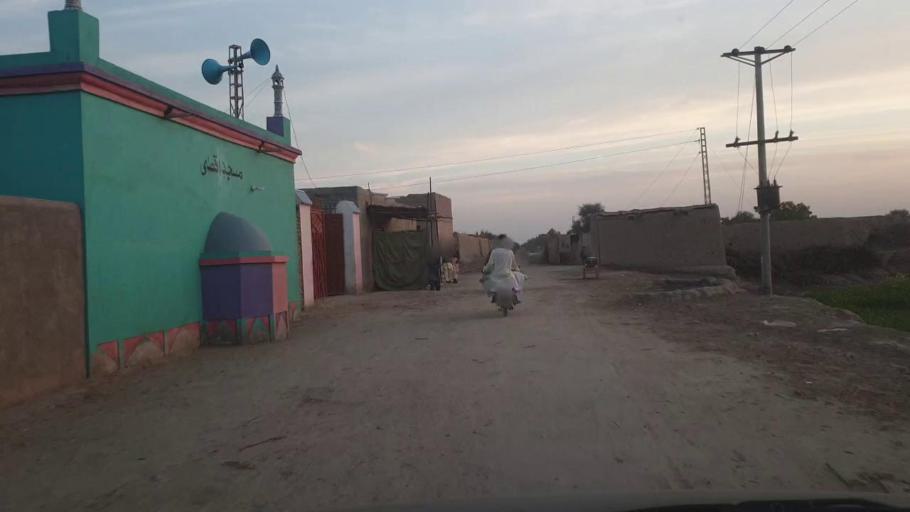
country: PK
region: Sindh
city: Shahpur Chakar
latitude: 26.0645
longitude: 68.5364
